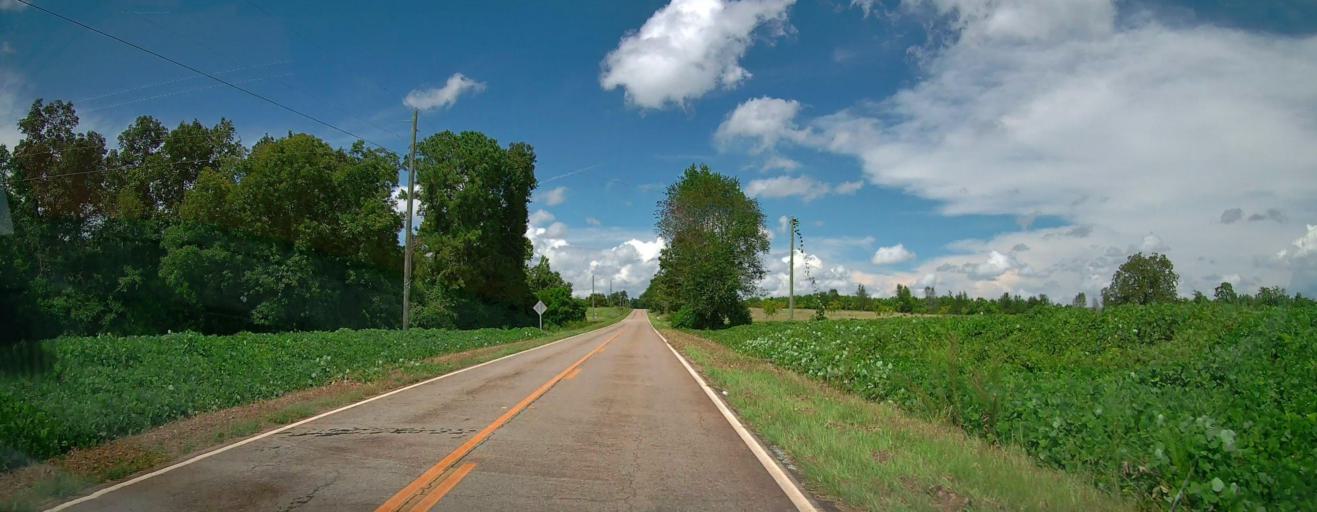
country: US
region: Georgia
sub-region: Peach County
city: Fort Valley
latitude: 32.5259
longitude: -83.8025
